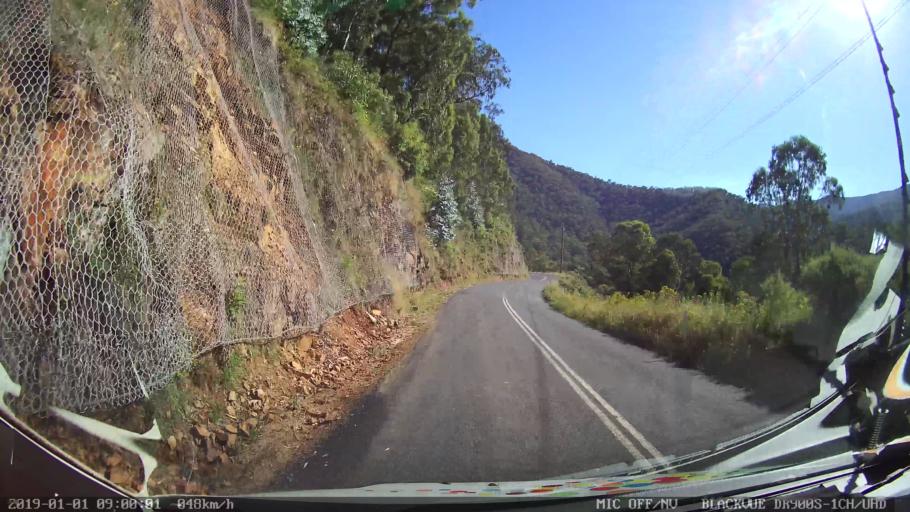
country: AU
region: New South Wales
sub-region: Snowy River
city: Jindabyne
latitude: -36.2378
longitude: 148.1806
